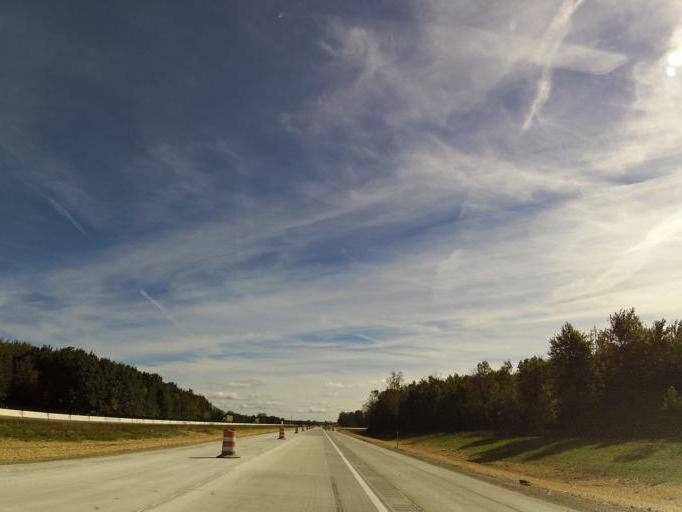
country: US
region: Michigan
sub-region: Macomb County
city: Memphis
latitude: 42.9790
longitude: -82.7765
